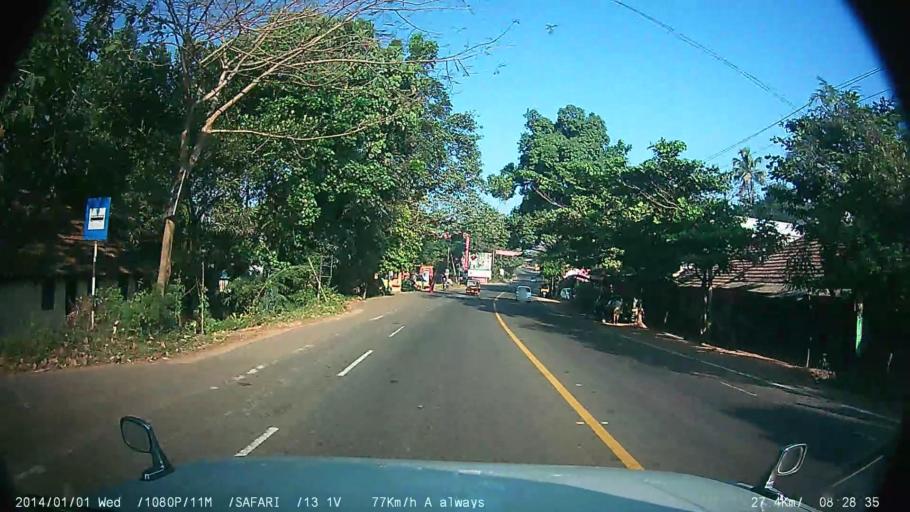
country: IN
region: Kerala
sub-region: Ernakulam
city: Perumbavoor
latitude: 10.0929
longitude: 76.4952
